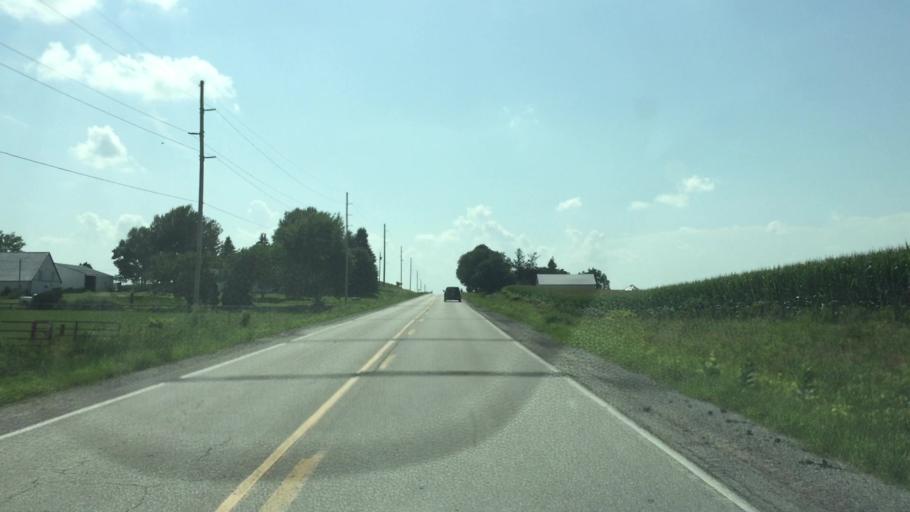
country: US
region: Iowa
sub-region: Linn County
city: Ely
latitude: 41.8474
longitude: -91.5816
